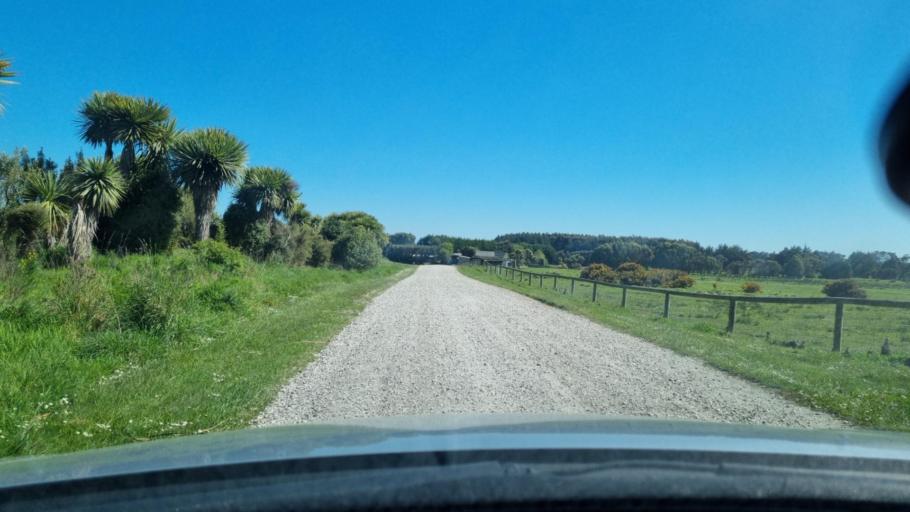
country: NZ
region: Southland
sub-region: Invercargill City
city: Invercargill
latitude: -46.4221
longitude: 168.2928
